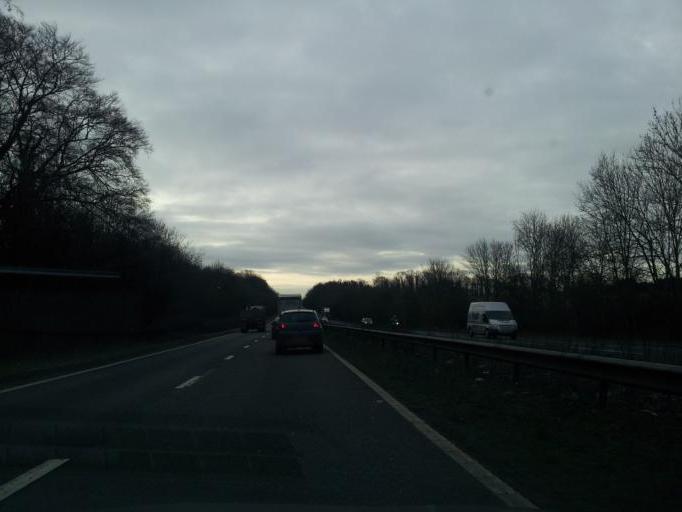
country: GB
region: England
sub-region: Lincolnshire
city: Grantham
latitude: 52.8259
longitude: -0.6298
